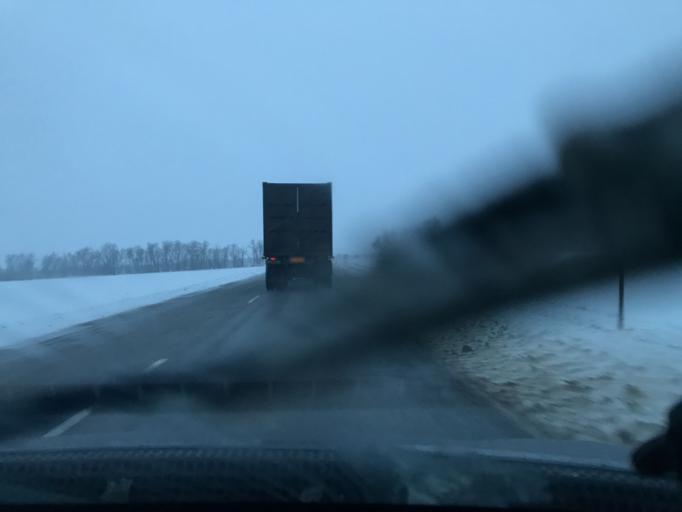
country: RU
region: Rostov
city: Letnik
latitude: 46.0621
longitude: 41.2073
